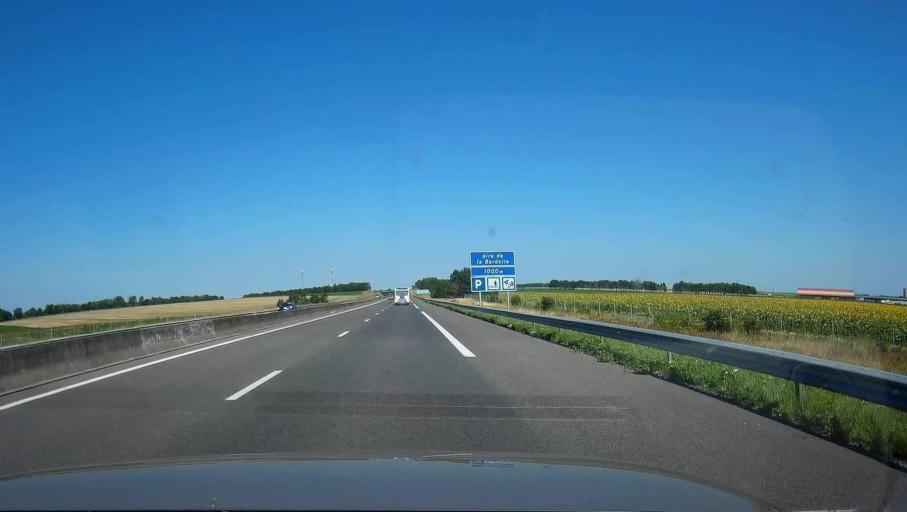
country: FR
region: Champagne-Ardenne
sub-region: Departement de la Marne
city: Compertrix
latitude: 48.8719
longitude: 4.2886
